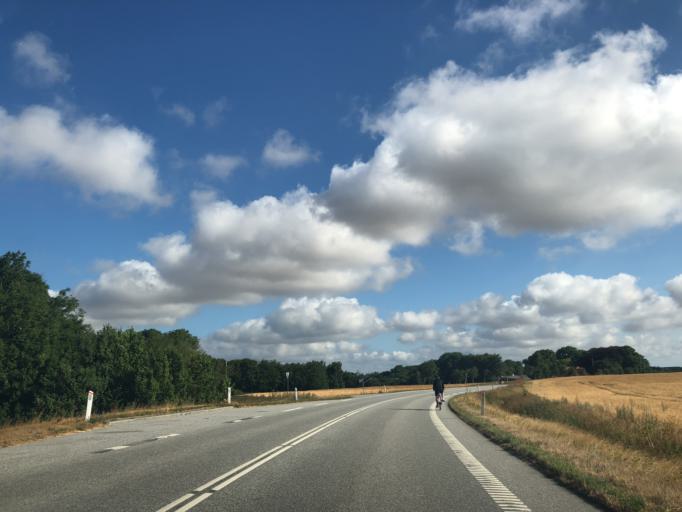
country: DK
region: Central Jutland
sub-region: Skive Kommune
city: Skive
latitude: 56.6393
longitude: 8.9196
